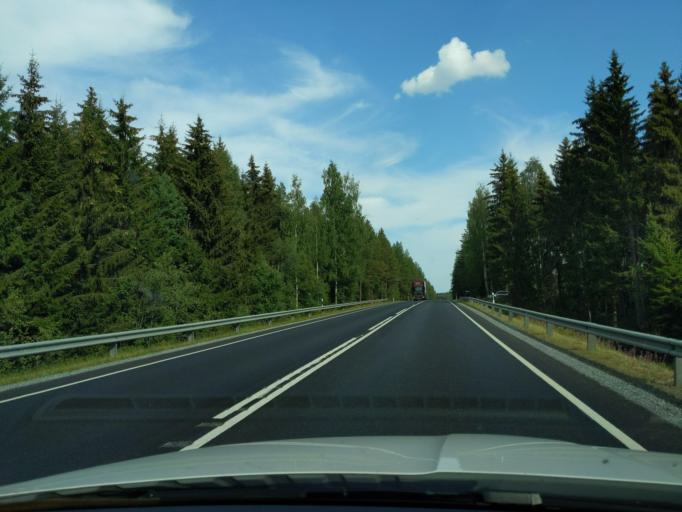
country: FI
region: Haeme
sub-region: Haemeenlinna
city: Tuulos
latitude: 61.1587
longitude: 24.6913
